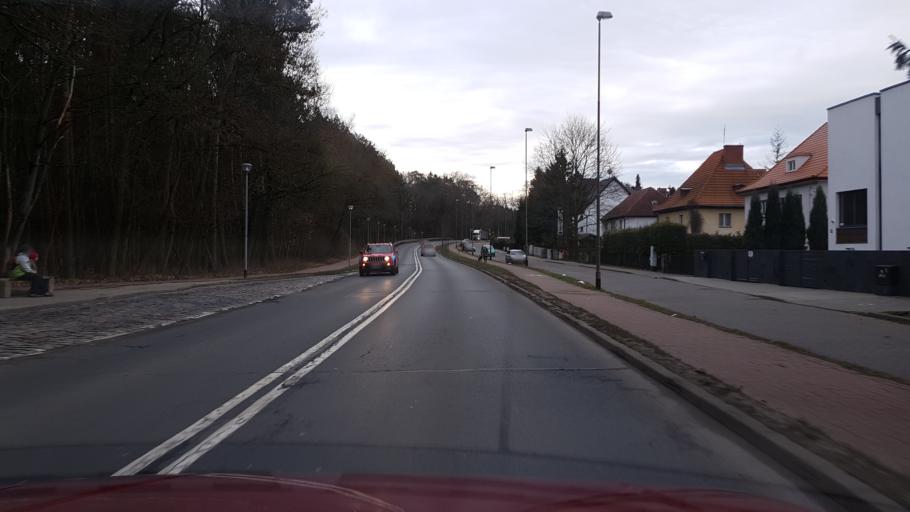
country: PL
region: West Pomeranian Voivodeship
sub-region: Szczecin
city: Szczecin
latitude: 53.4770
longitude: 14.4854
